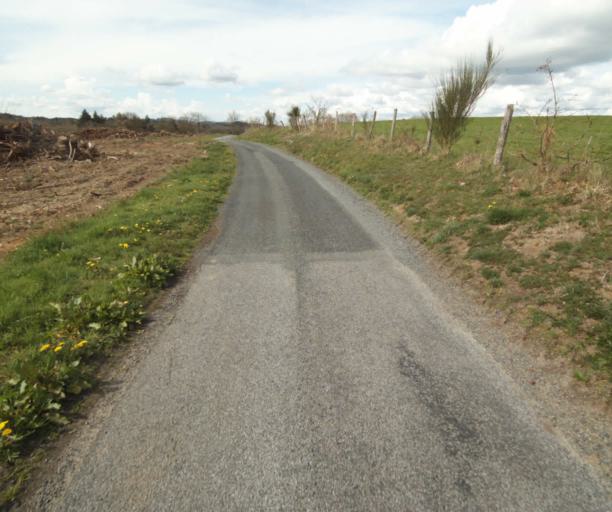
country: FR
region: Limousin
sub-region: Departement de la Correze
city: Correze
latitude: 45.3687
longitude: 1.9056
